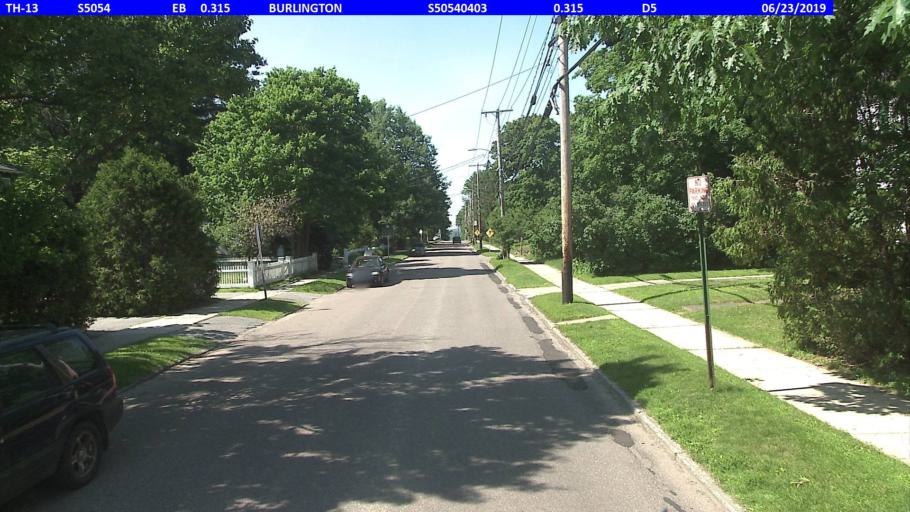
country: US
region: Vermont
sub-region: Chittenden County
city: Burlington
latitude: 44.4852
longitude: -73.2016
